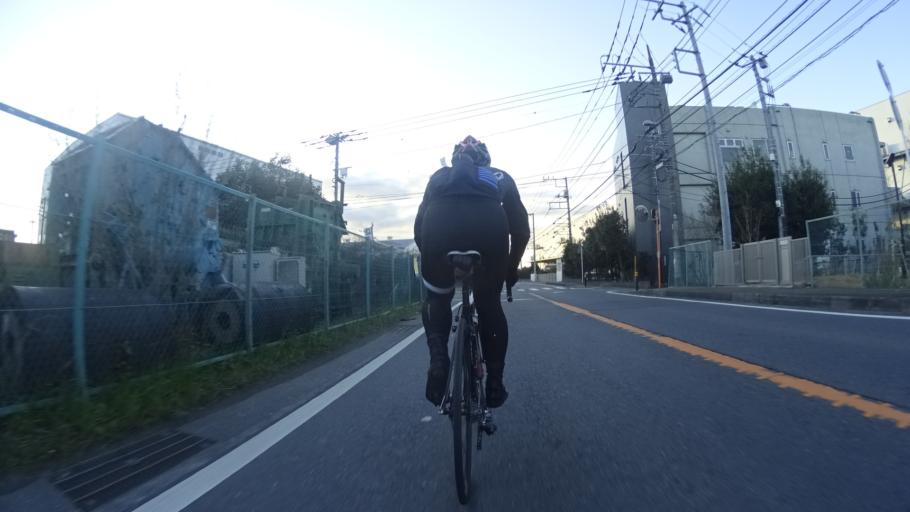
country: JP
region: Kanagawa
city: Atsugi
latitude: 35.4560
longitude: 139.3685
